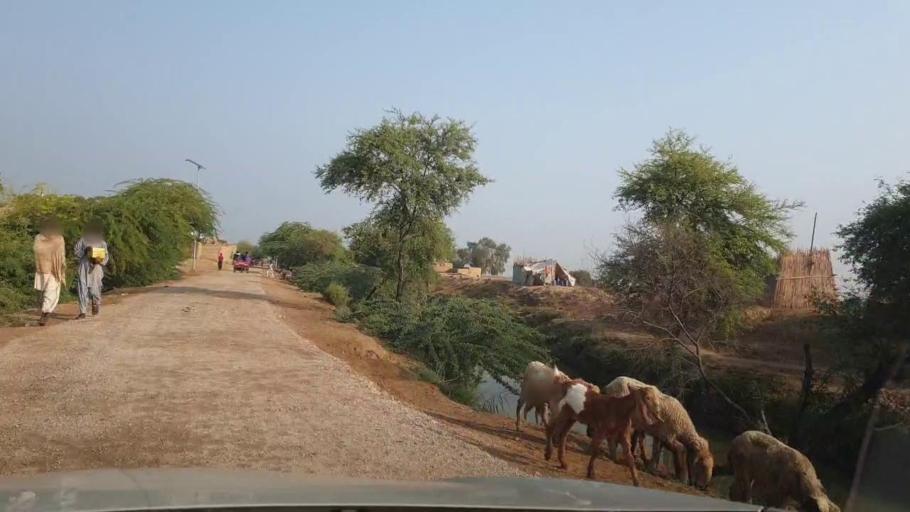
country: PK
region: Sindh
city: Sehwan
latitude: 26.3487
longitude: 67.7232
